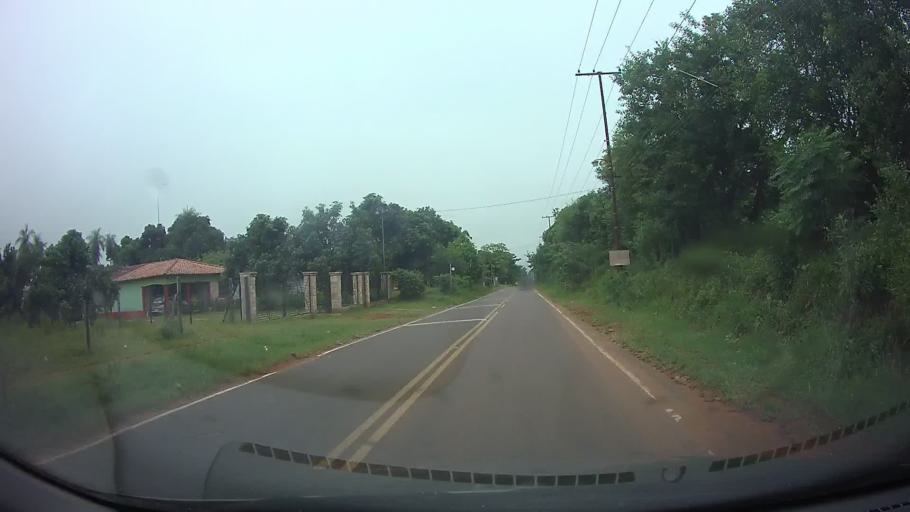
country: PY
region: Central
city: Itaugua
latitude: -25.3756
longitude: -57.3487
